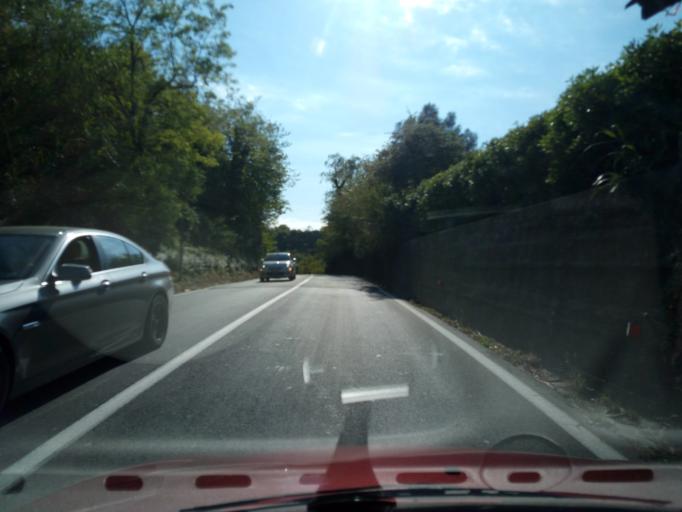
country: IT
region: Liguria
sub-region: Provincia di Genova
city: Cogoleto
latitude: 44.3991
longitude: 8.6643
